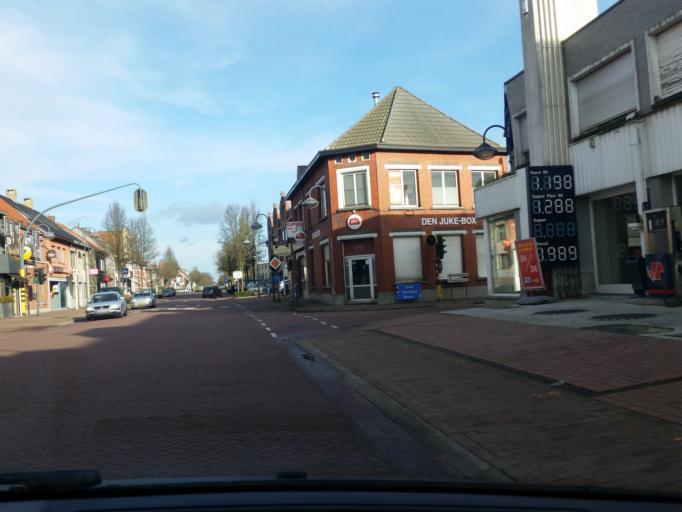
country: BE
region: Flanders
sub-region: Provincie Antwerpen
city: Wuustwezel
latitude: 51.3890
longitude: 4.5905
